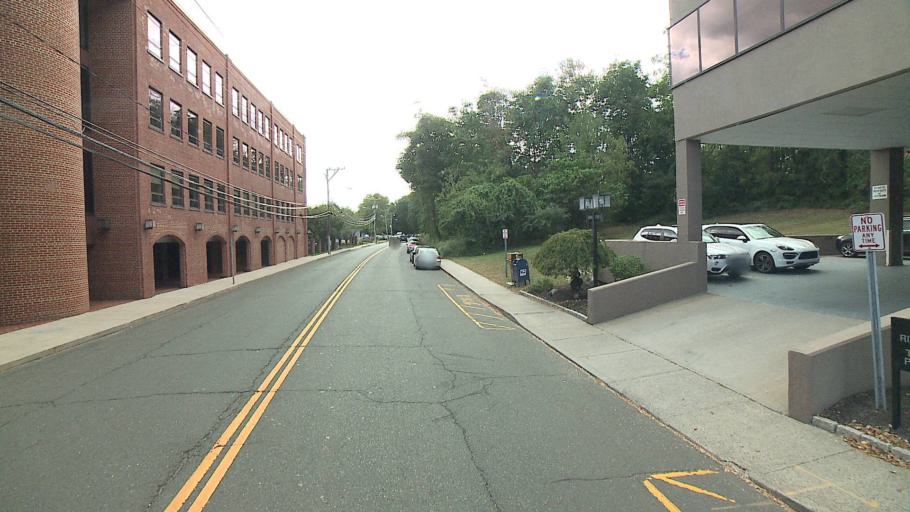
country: US
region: Connecticut
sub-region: Fairfield County
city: Westport
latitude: 41.1308
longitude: -73.3688
